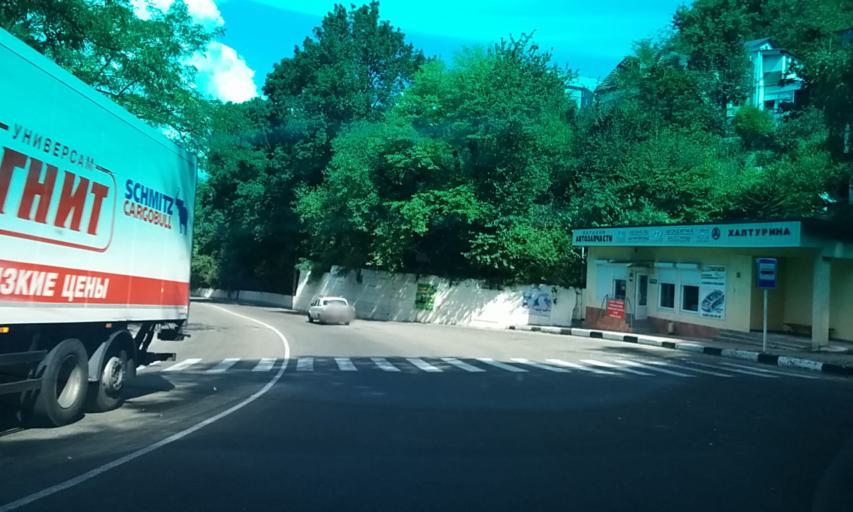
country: RU
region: Krasnodarskiy
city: Tuapse
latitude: 44.1045
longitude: 39.0638
